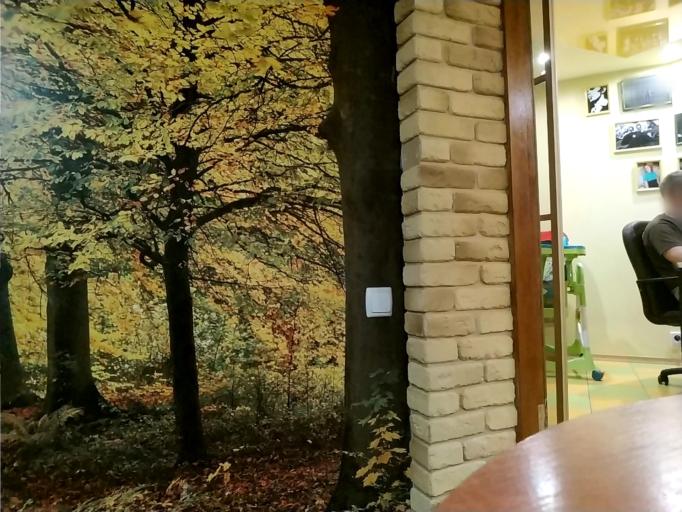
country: RU
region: Tverskaya
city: Zapadnaya Dvina
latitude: 56.3239
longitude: 31.9137
